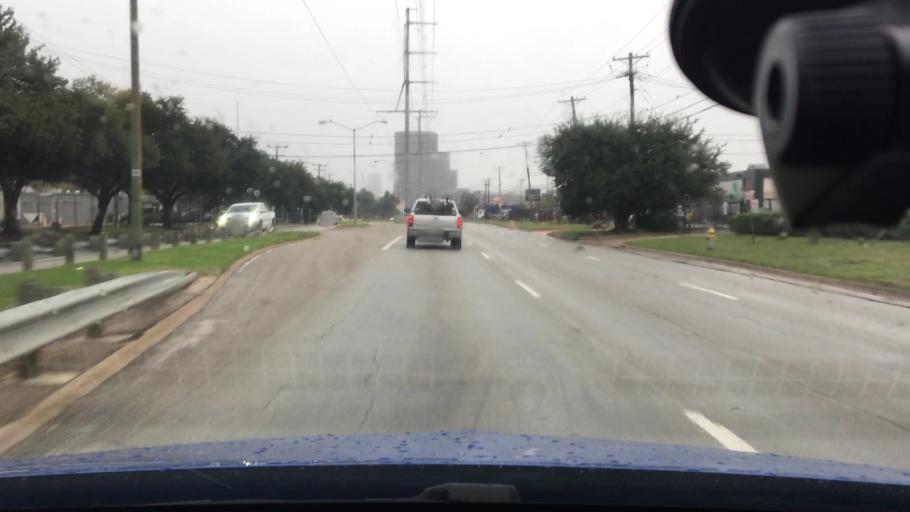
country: US
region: Texas
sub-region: Dallas County
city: Dallas
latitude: 32.8084
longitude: -96.8587
